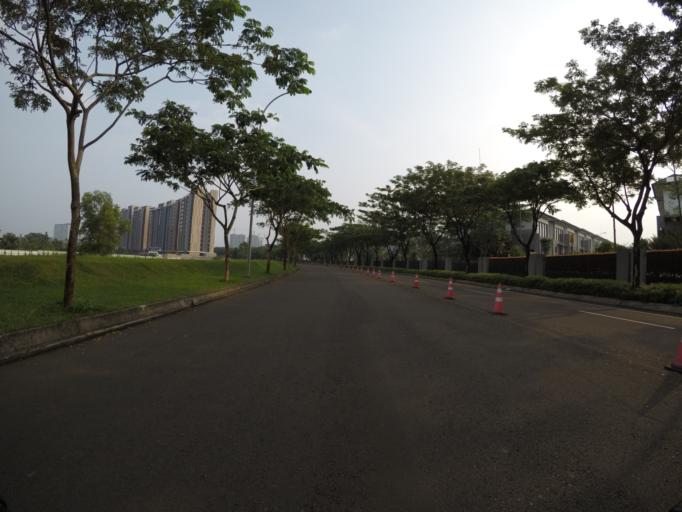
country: ID
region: West Java
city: Serpong
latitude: -6.2934
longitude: 106.6512
